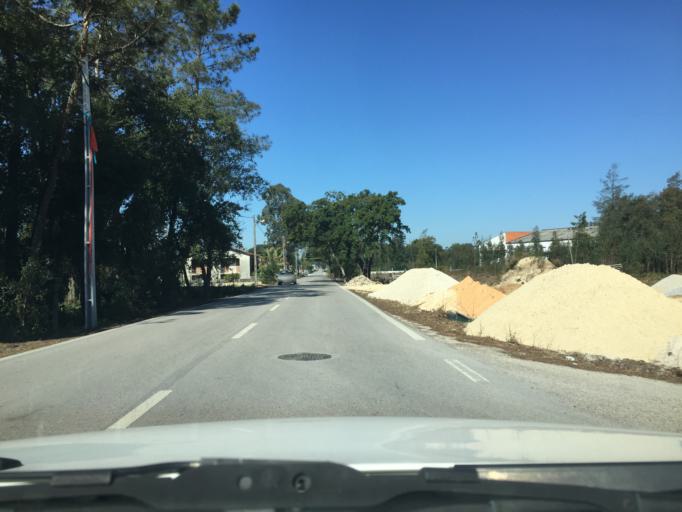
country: PT
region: Coimbra
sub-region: Cantanhede
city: Cantanhede
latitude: 40.4184
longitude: -8.5627
